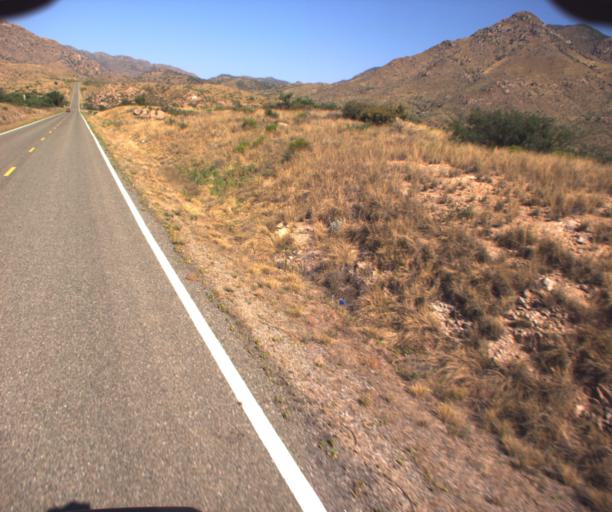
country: US
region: Arizona
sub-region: Graham County
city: Swift Trail Junction
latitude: 32.5601
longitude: -109.7545
